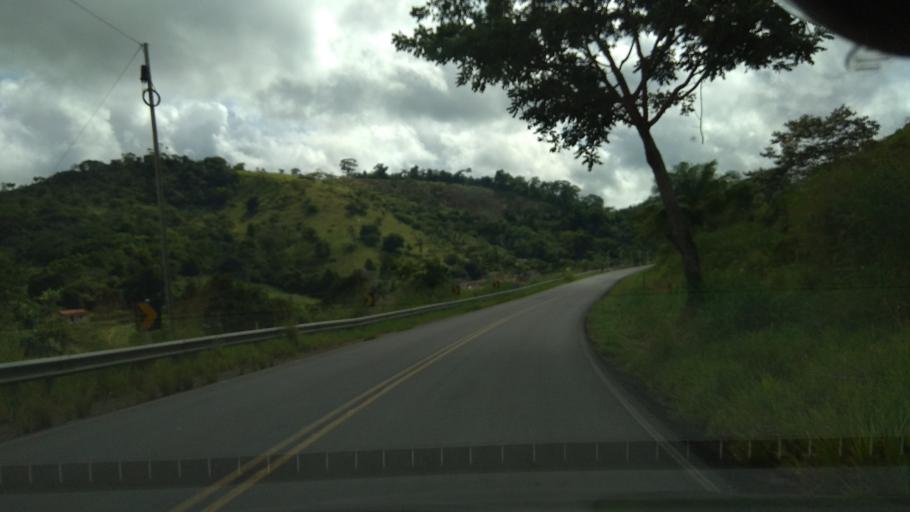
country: BR
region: Bahia
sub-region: Mutuipe
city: Mutuipe
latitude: -13.1860
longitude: -39.4415
